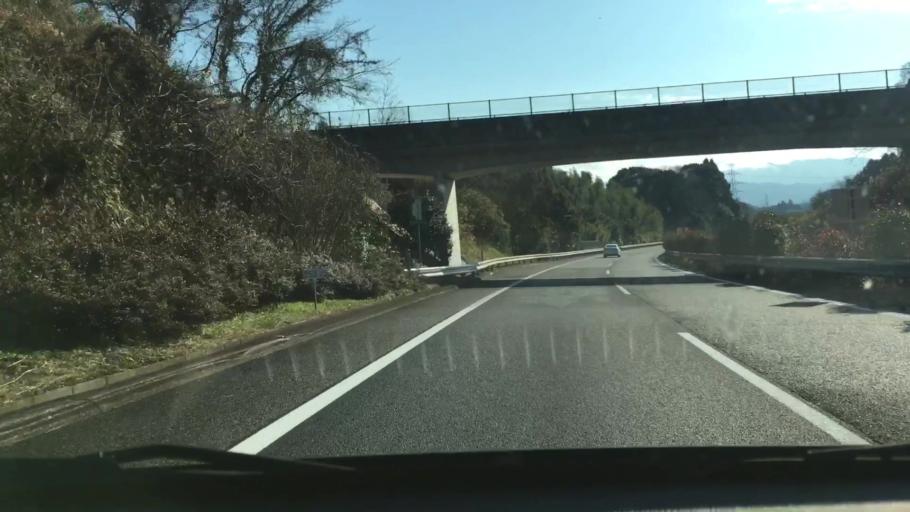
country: JP
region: Kumamoto
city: Hitoyoshi
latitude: 32.2188
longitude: 130.7803
